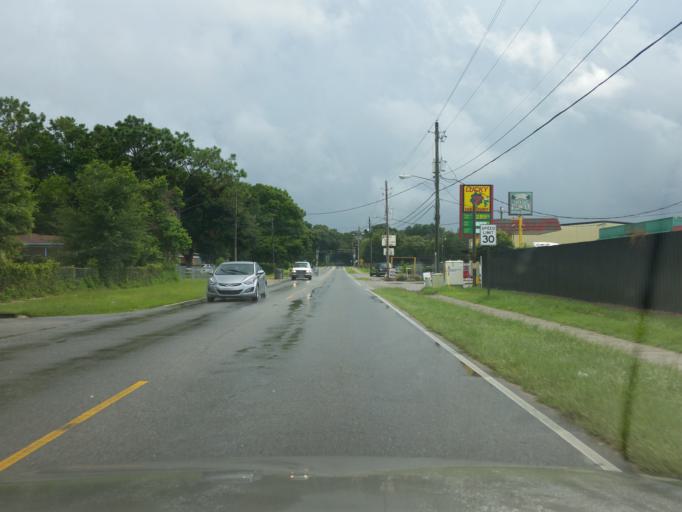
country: US
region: Florida
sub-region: Escambia County
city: Brent
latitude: 30.4537
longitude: -87.2571
